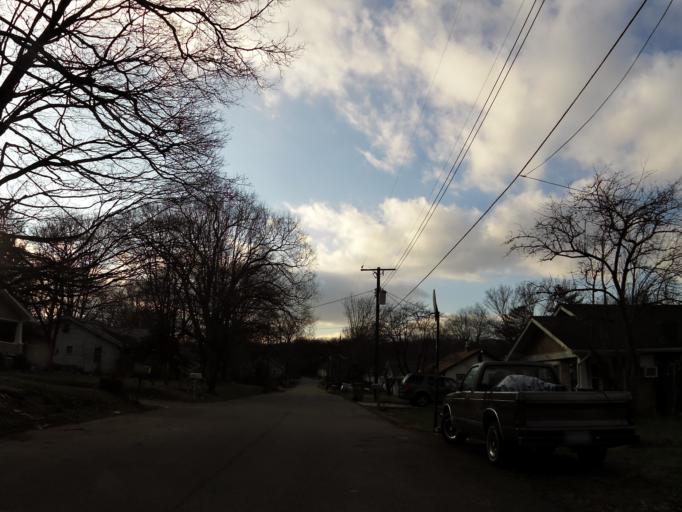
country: US
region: Tennessee
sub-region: Knox County
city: Knoxville
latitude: 35.9510
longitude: -83.8901
